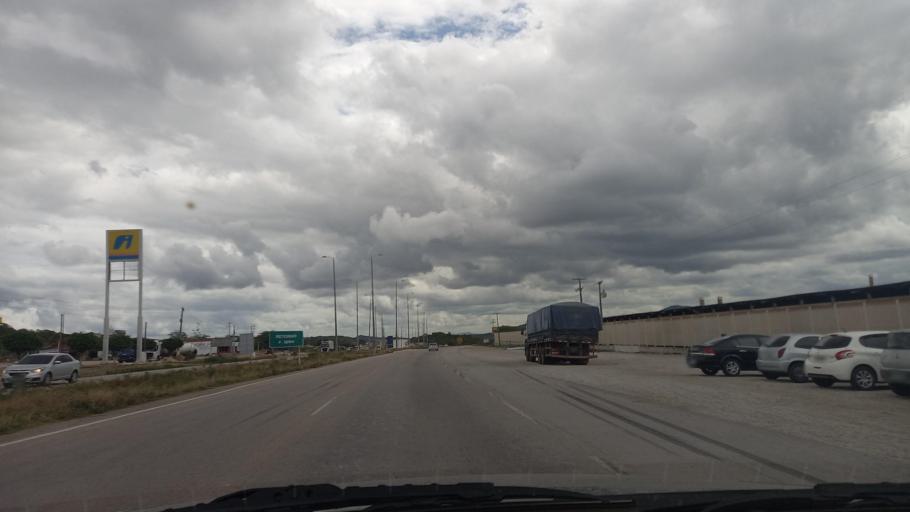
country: BR
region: Pernambuco
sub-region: Caruaru
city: Caruaru
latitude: -8.3206
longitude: -36.0785
